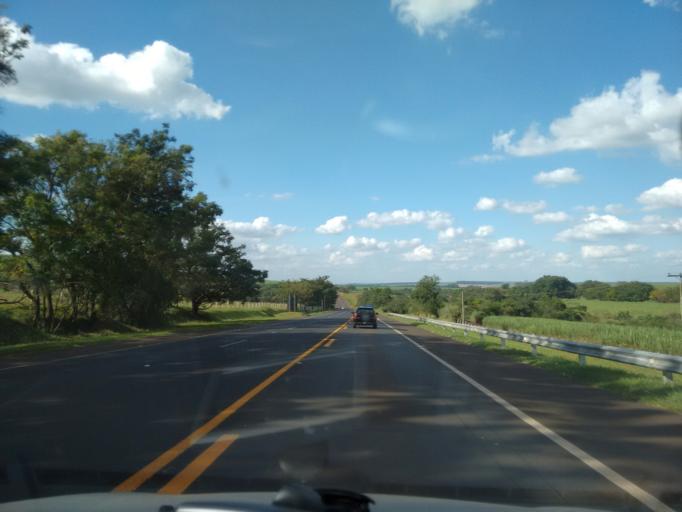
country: BR
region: Sao Paulo
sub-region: Americo Brasiliense
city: Americo Brasiliense
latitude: -21.7605
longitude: -48.0764
